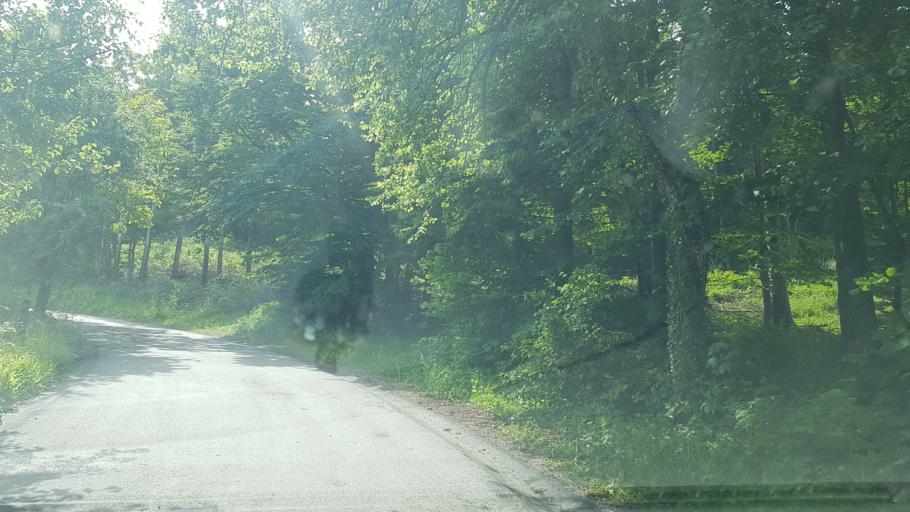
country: SI
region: Dobrna
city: Dobrna
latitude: 46.3819
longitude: 15.1796
